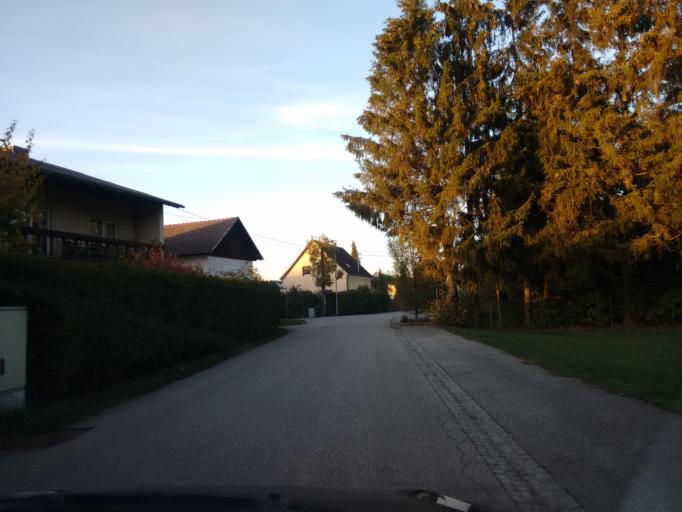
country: AT
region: Upper Austria
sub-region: Wels-Land
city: Gunskirchen
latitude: 48.1509
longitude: 13.9660
